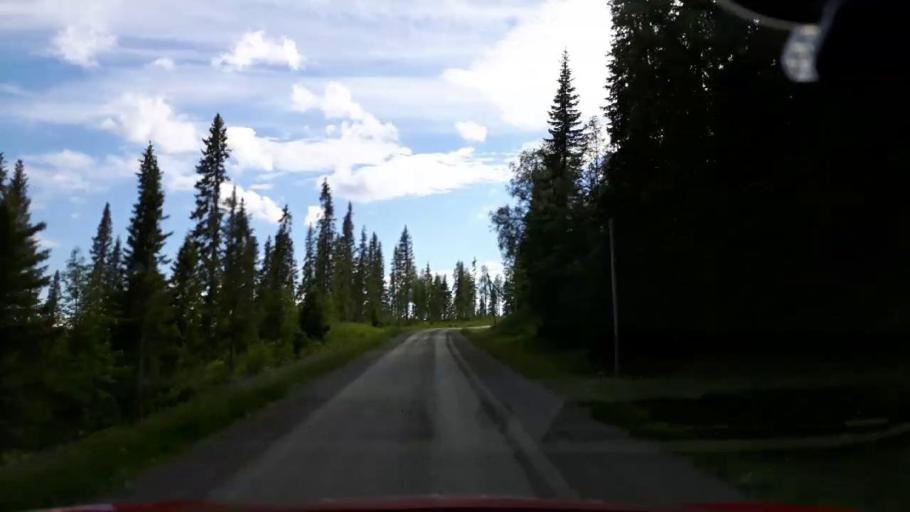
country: SE
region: Jaemtland
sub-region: Krokoms Kommun
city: Valla
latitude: 63.8446
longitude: 14.0766
